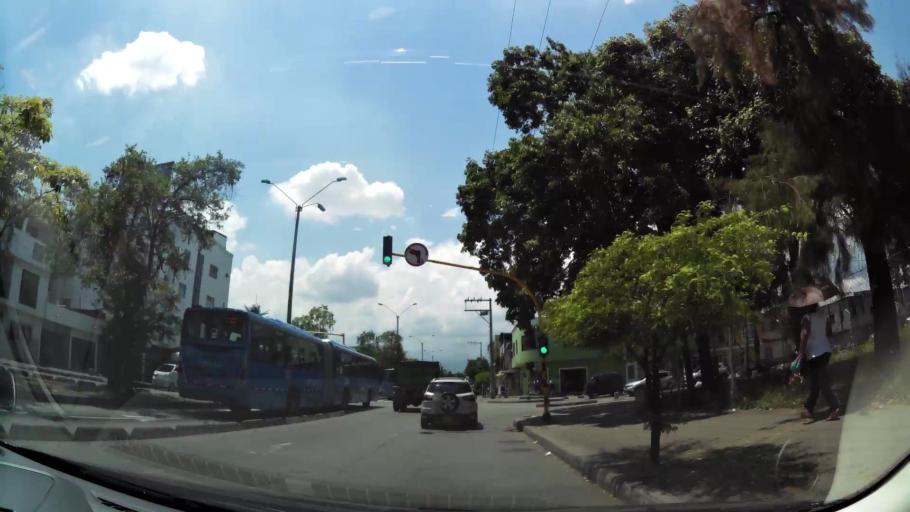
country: CO
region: Valle del Cauca
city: Cali
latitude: 3.4434
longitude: -76.4943
